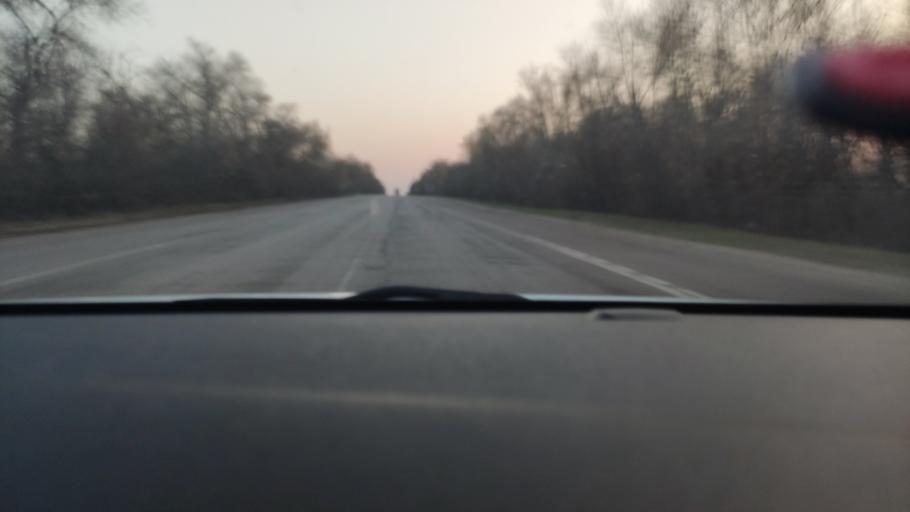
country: RU
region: Voronezj
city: Uryv-Pokrovka
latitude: 51.1478
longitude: 39.0597
